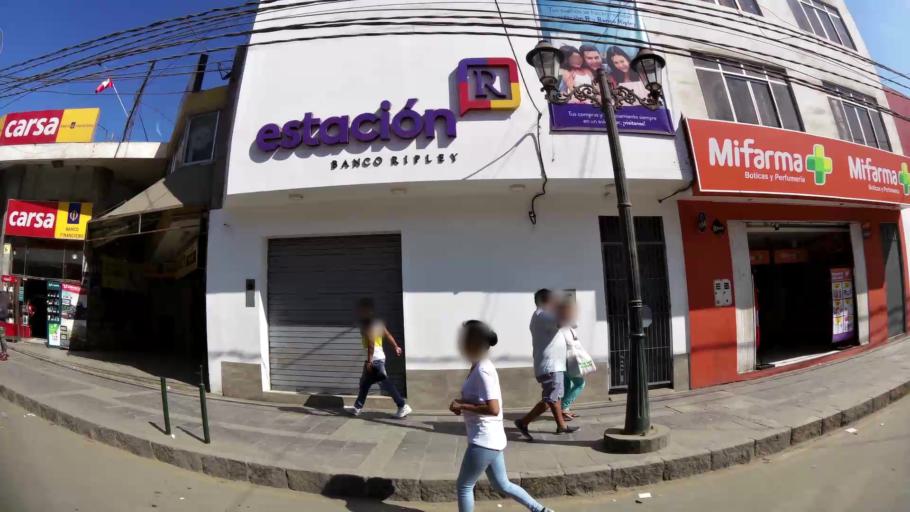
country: PE
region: Ica
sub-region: Provincia de Chincha
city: Chincha Alta
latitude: -13.4174
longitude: -76.1353
